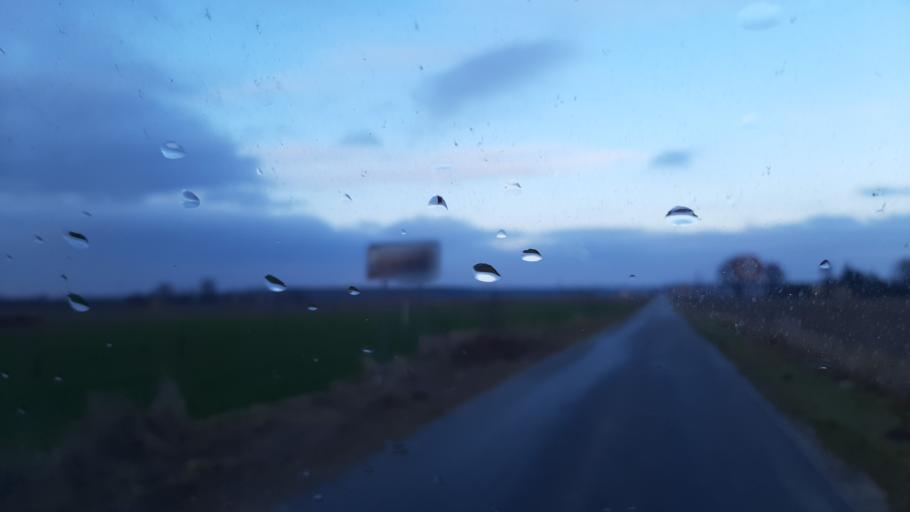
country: PL
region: Lublin Voivodeship
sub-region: Powiat lubelski
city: Jastkow
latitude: 51.3560
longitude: 22.3952
